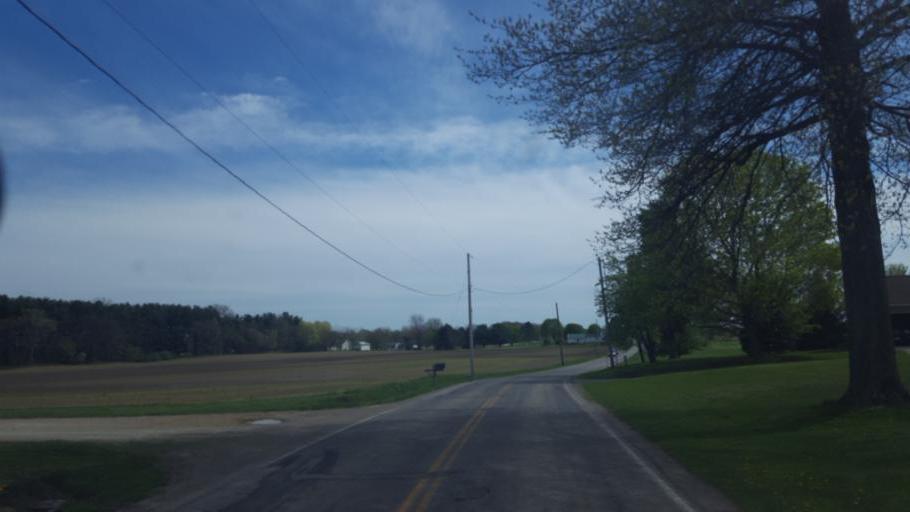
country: US
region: Ohio
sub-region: Richland County
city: Shelby
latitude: 40.8901
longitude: -82.6224
